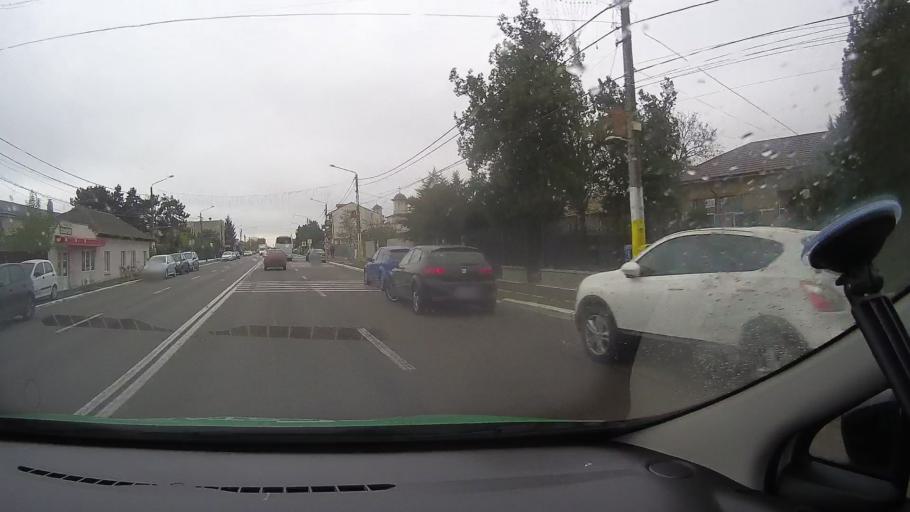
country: RO
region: Constanta
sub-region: Comuna Valu lui Traian
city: Valu lui Traian
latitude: 44.1648
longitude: 28.4810
